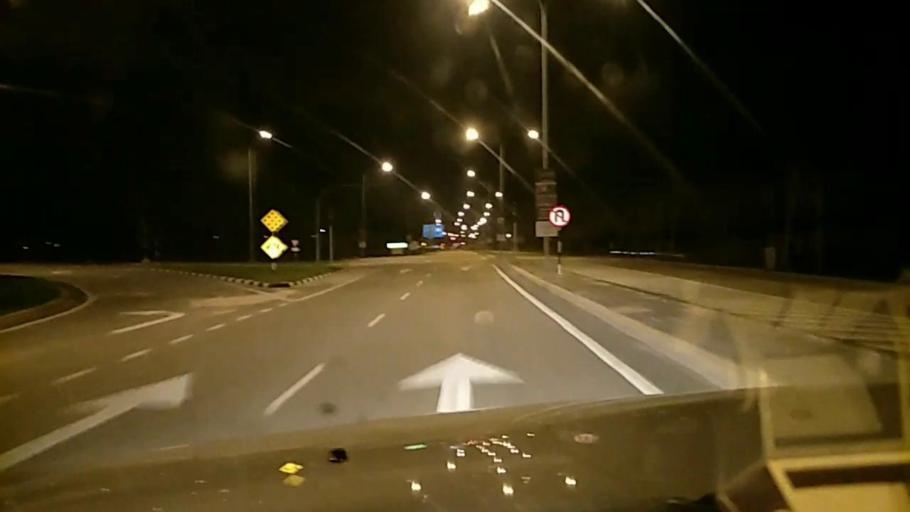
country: MY
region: Selangor
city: Ladang Seri Kundang
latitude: 3.2508
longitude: 101.4706
